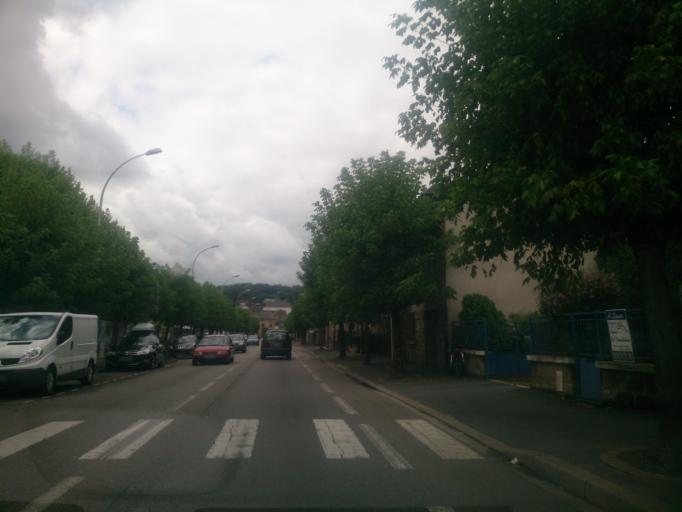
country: FR
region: Limousin
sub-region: Departement de la Correze
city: Brive-la-Gaillarde
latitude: 45.1539
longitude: 1.5377
